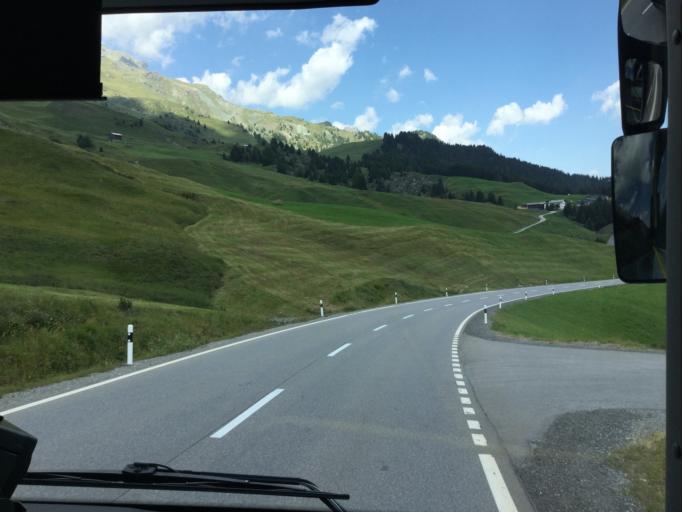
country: CH
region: Grisons
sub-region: Maloja District
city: Silvaplana
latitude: 46.4795
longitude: 9.6422
